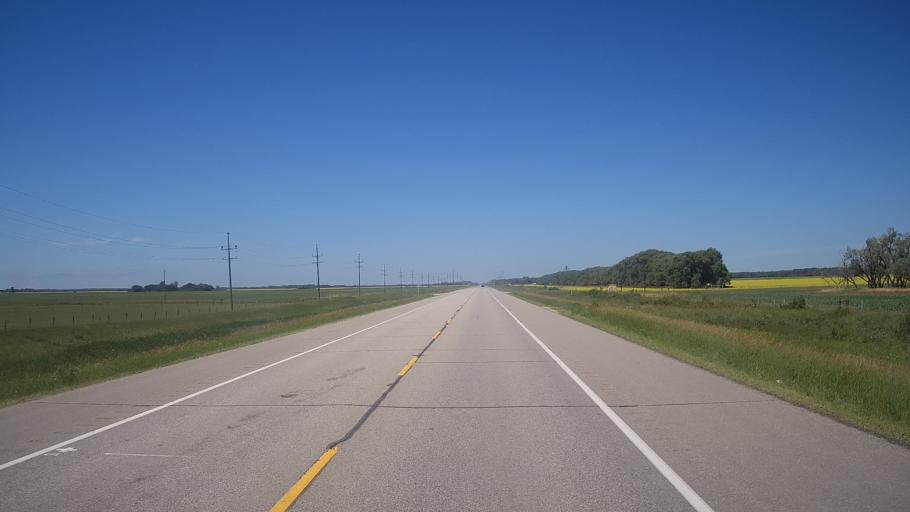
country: CA
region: Manitoba
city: Neepawa
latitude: 50.2257
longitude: -99.0625
